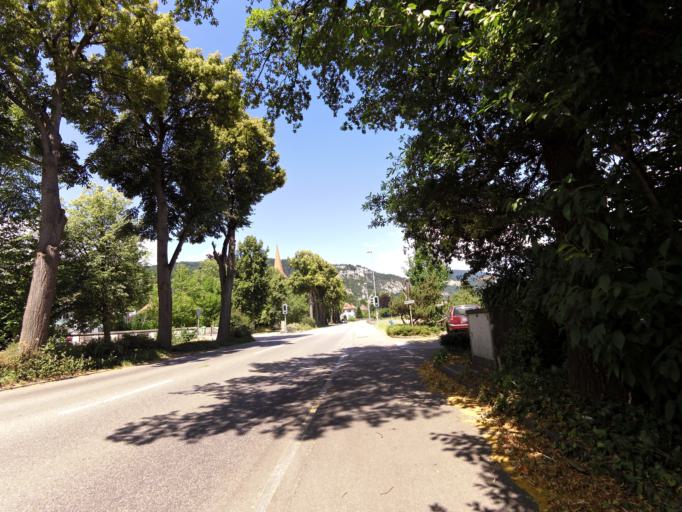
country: CH
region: Solothurn
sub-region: Bezirk Thal
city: Balsthal
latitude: 47.3116
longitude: 7.6901
